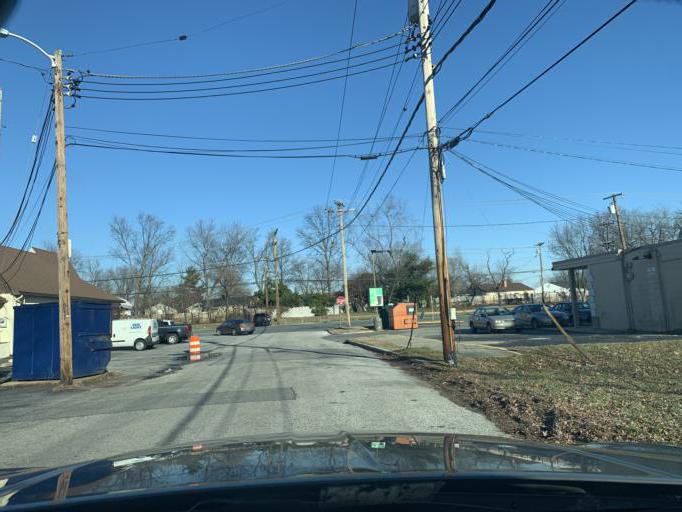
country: US
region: Maryland
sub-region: Anne Arundel County
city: Glen Burnie
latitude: 39.1532
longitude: -76.6185
